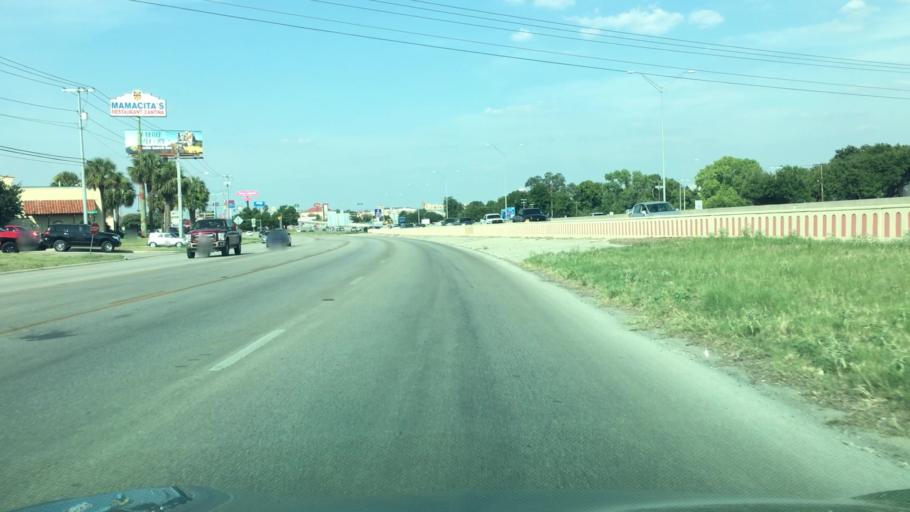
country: US
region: Texas
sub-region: Comal County
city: New Braunfels
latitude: 29.6948
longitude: -98.1038
